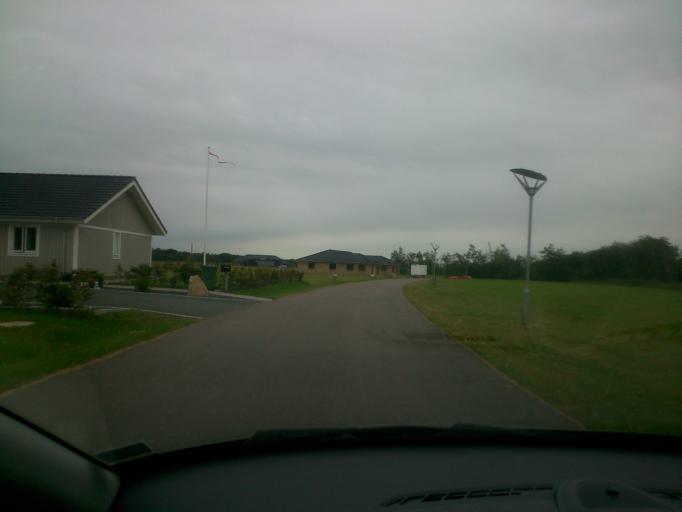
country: DK
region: Central Jutland
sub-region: Ringkobing-Skjern Kommune
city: Skjern
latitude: 55.9602
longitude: 8.4789
